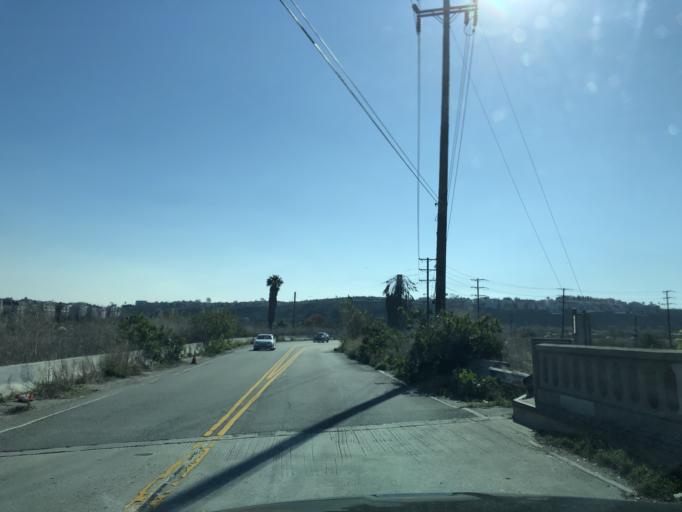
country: US
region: California
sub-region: Los Angeles County
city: Marina del Rey
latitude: 33.9741
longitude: -118.4335
